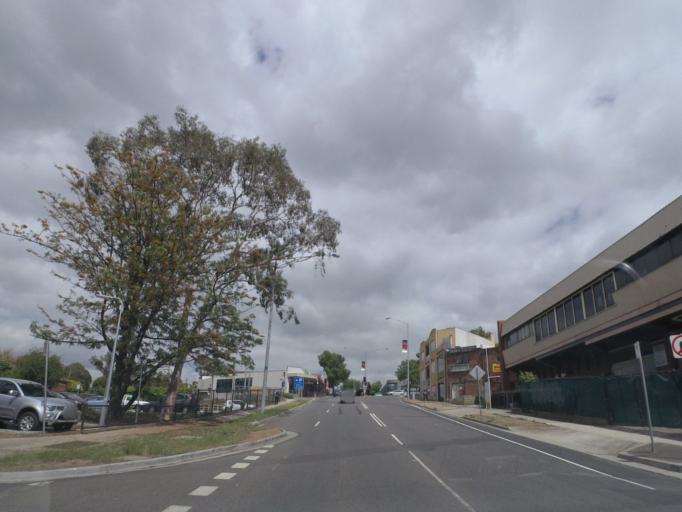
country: AU
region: Victoria
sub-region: Banyule
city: Greensborough
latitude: -37.7047
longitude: 145.1037
